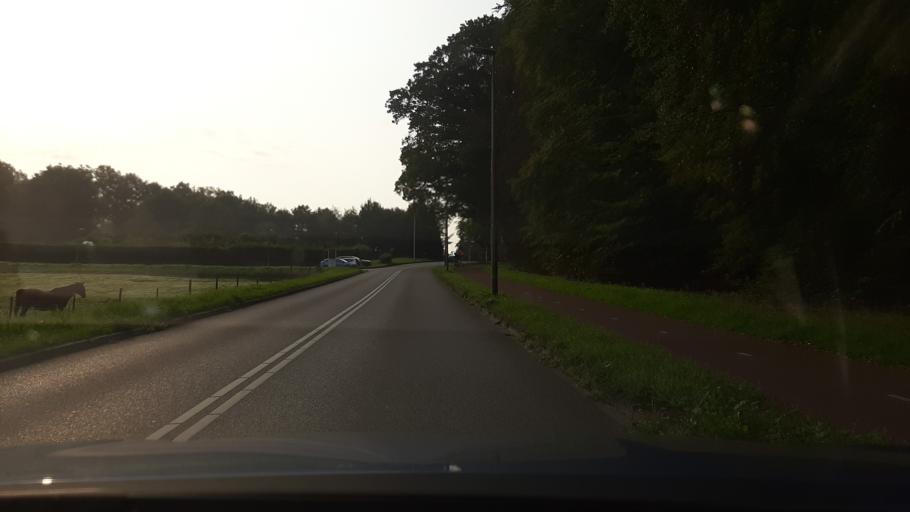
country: NL
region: Gelderland
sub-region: Gemeente Arnhem
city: Burgemeesterswijk
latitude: 51.9962
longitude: 5.9084
